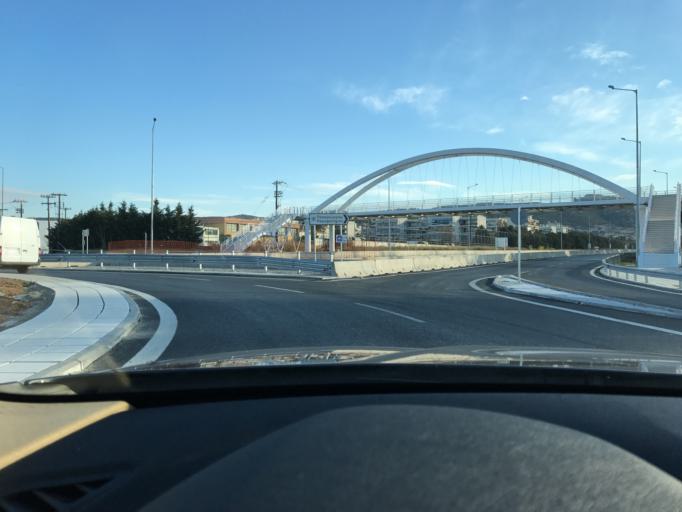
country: GR
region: Central Macedonia
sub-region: Nomos Thessalonikis
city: Efkarpia
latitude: 40.6801
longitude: 22.9469
